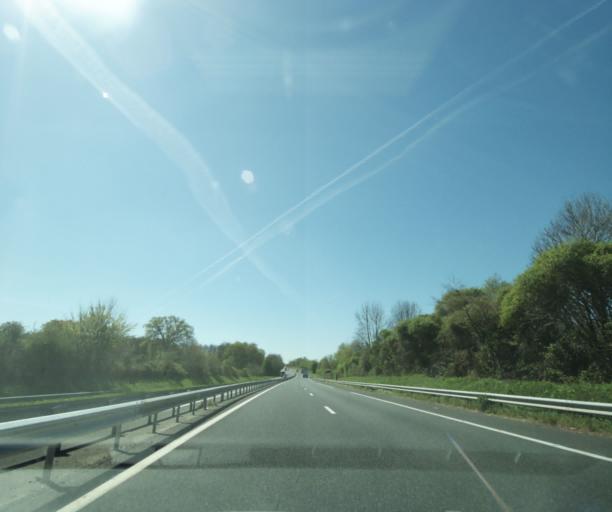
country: FR
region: Centre
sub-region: Departement de l'Indre
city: Chantome
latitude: 46.4292
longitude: 1.4757
